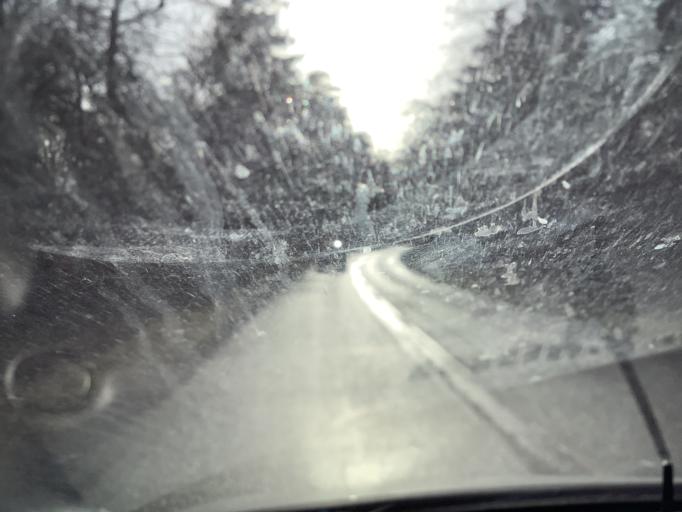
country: GB
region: England
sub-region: Hampshire
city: Brockenhurst
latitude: 50.8205
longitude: -1.5366
